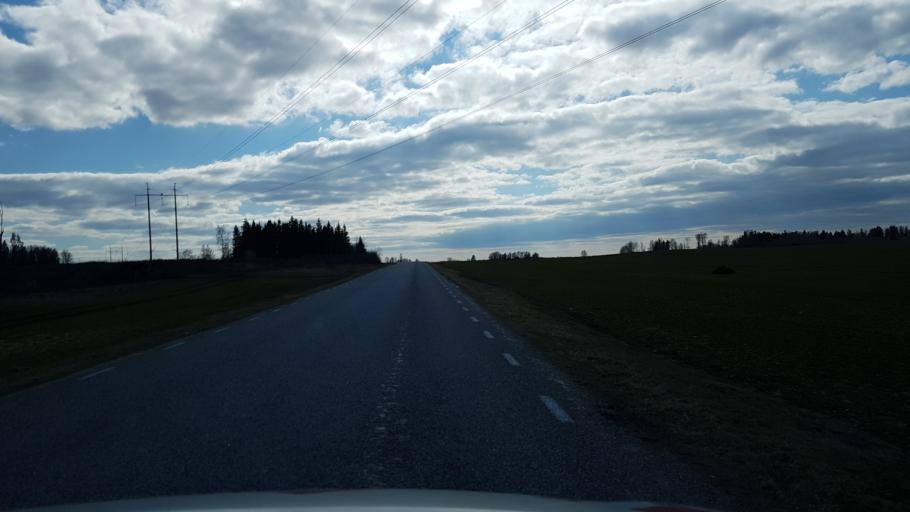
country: EE
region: Laeaene-Virumaa
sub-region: Kadrina vald
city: Kadrina
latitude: 59.3020
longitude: 26.2206
